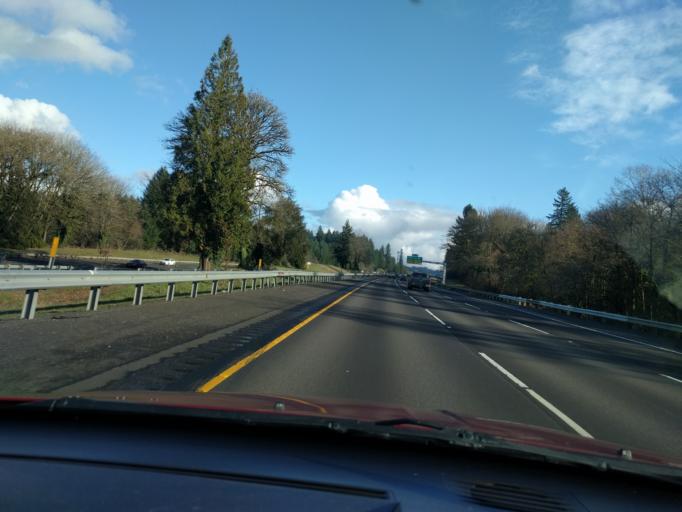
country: US
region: Oregon
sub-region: Clackamas County
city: Stafford
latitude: 45.3732
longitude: -122.7261
